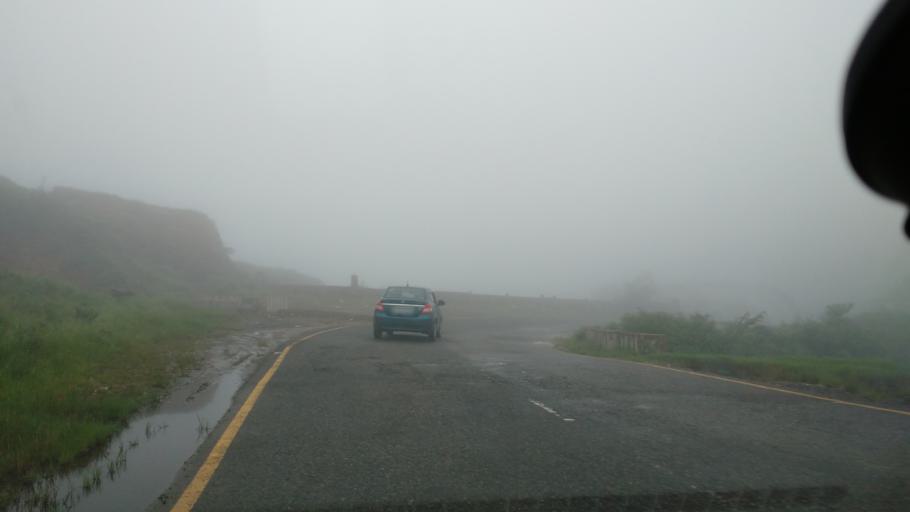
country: IN
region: Meghalaya
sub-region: East Khasi Hills
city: Cherrapunji
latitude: 25.2880
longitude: 91.7157
